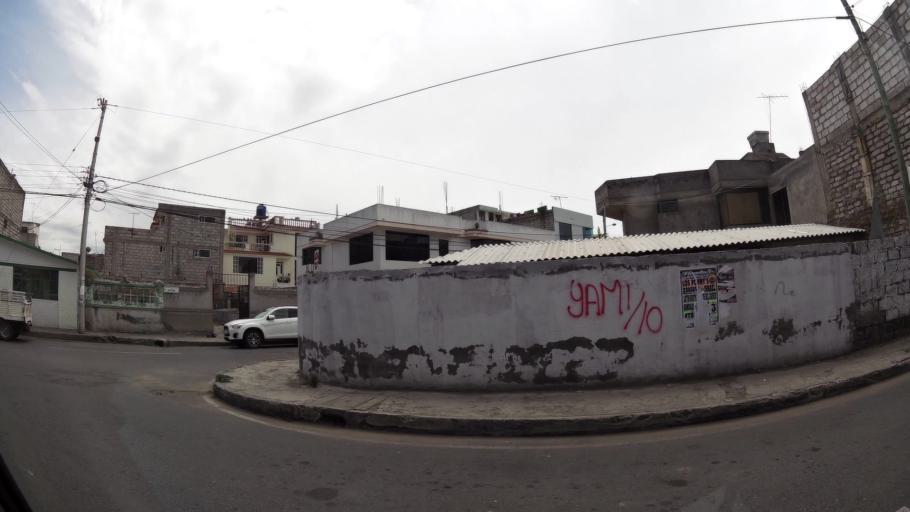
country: EC
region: Cotopaxi
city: San Miguel de Salcedo
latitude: -1.0460
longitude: -78.5910
